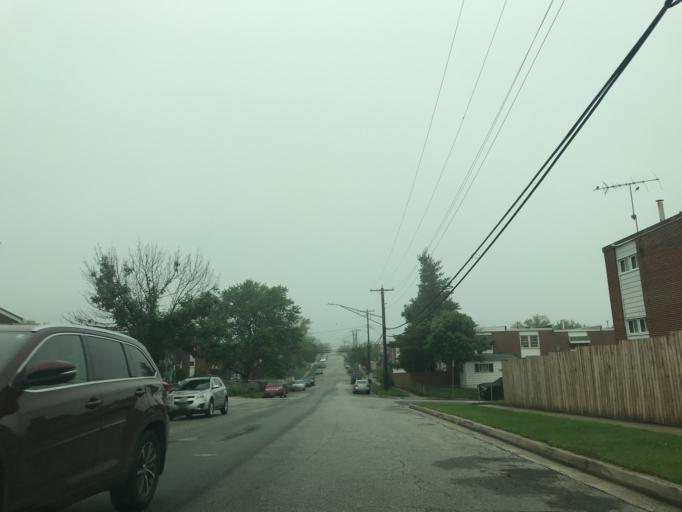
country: US
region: Maryland
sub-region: Baltimore County
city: Rosedale
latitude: 39.2959
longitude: -76.5123
